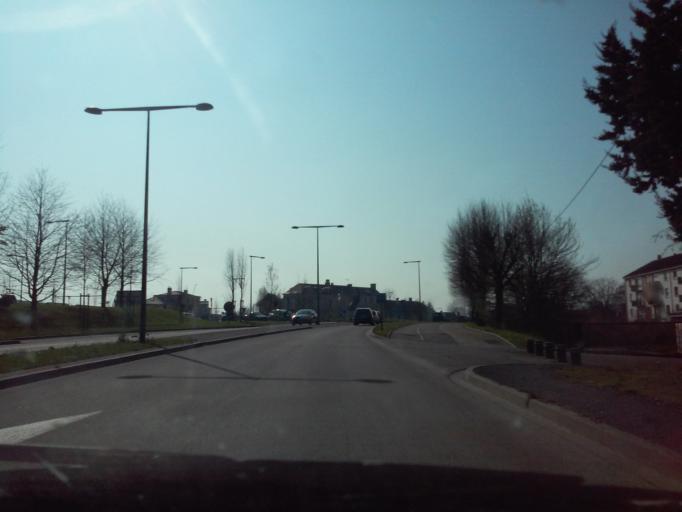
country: FR
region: Lower Normandy
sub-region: Departement du Calvados
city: Bayeux
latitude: 49.2706
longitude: -0.6955
